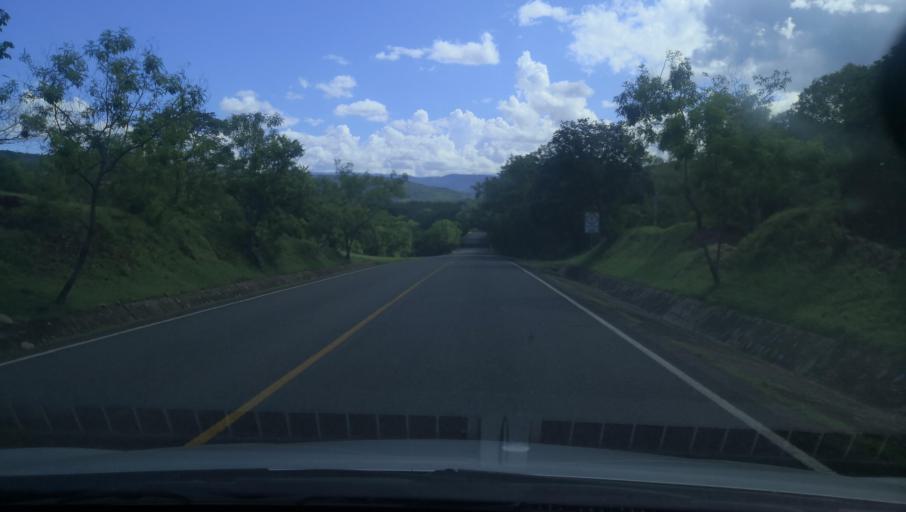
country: NI
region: Madriz
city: Somoto
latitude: 13.4664
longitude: -86.6546
